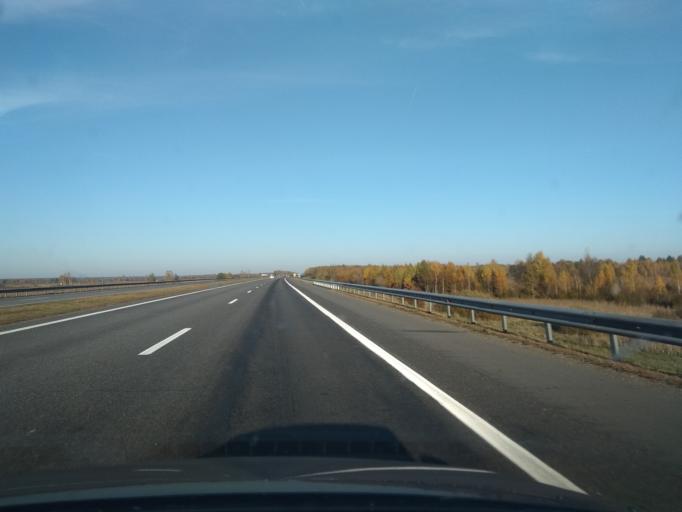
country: BY
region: Brest
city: Nyakhachava
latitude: 52.6055
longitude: 25.1646
